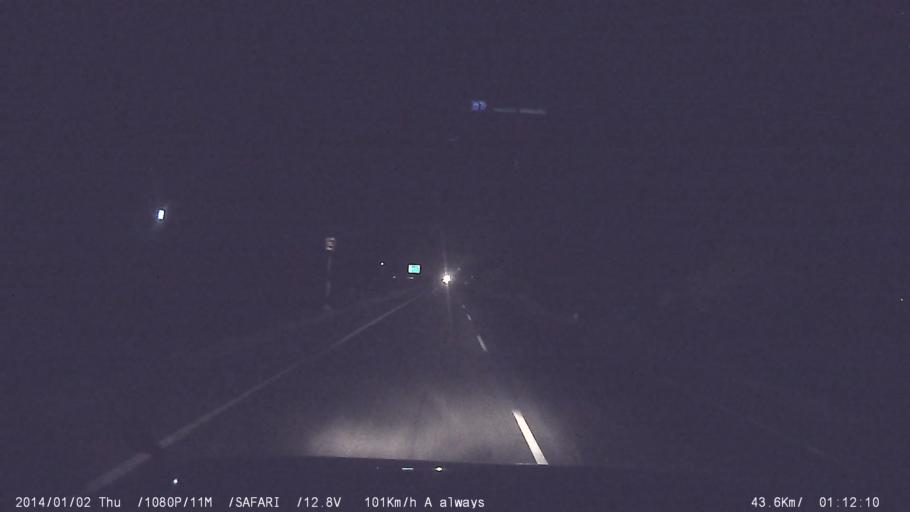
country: IN
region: Tamil Nadu
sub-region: Coimbatore
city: Singanallur
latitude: 10.9650
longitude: 77.0319
